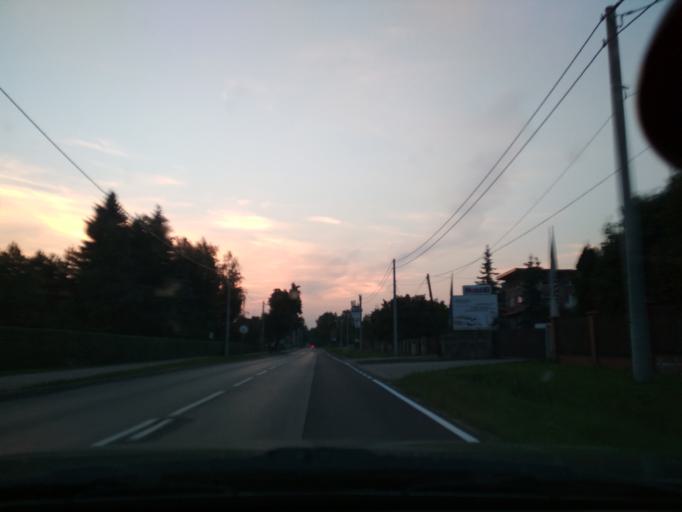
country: PL
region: Silesian Voivodeship
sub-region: Powiat zawiercianski
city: Ogrodzieniec
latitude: 50.4581
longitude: 19.5001
